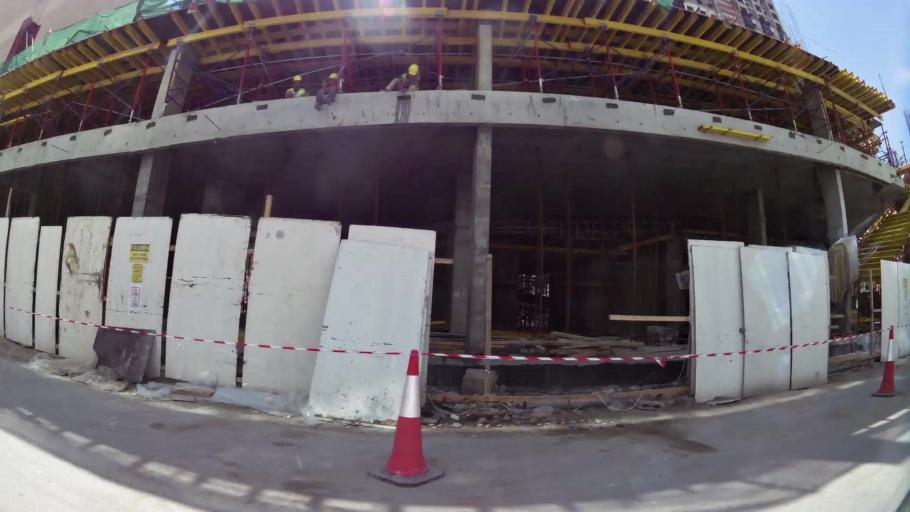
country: BH
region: Manama
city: Manama
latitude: 26.2200
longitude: 50.6103
